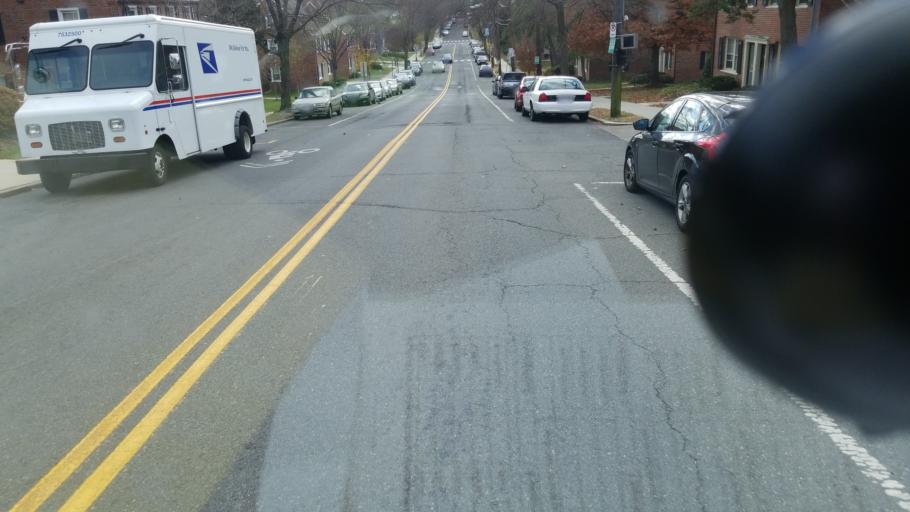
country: US
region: Maryland
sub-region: Prince George's County
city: Silver Hill
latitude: 38.8642
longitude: -76.9523
